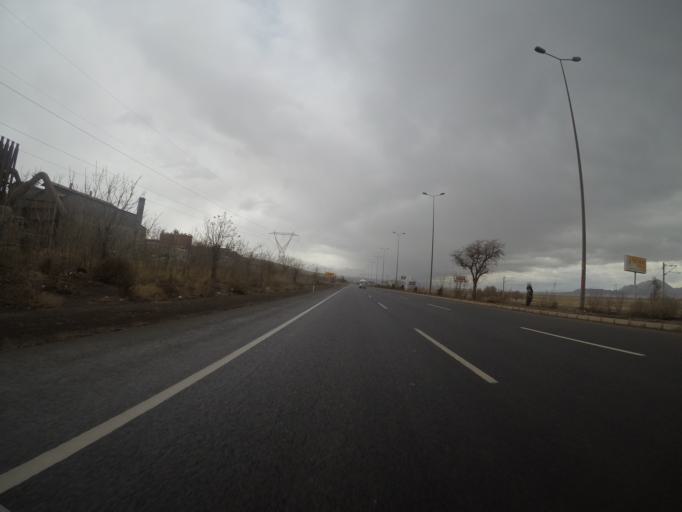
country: TR
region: Kayseri
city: Incesu
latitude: 38.7115
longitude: 35.2632
